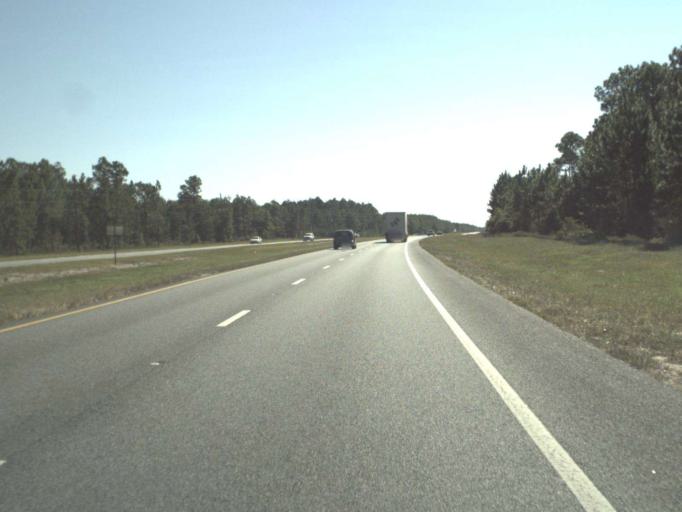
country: US
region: Florida
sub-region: Walton County
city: Seaside
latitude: 30.3501
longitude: -86.0825
